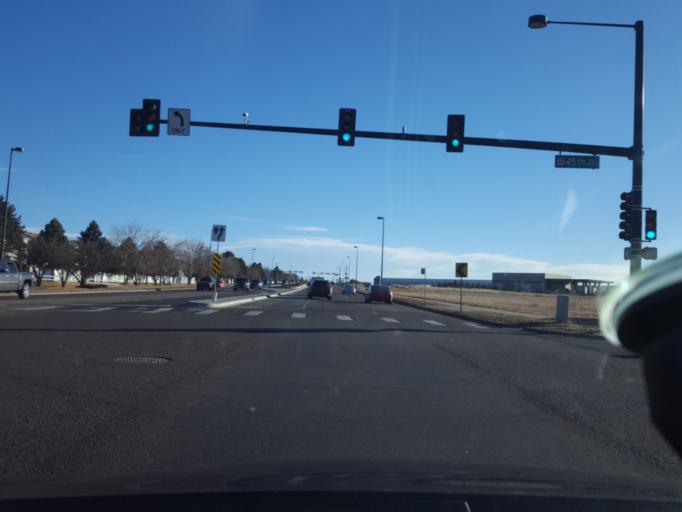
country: US
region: Colorado
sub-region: Adams County
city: Aurora
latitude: 39.7781
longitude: -104.7722
